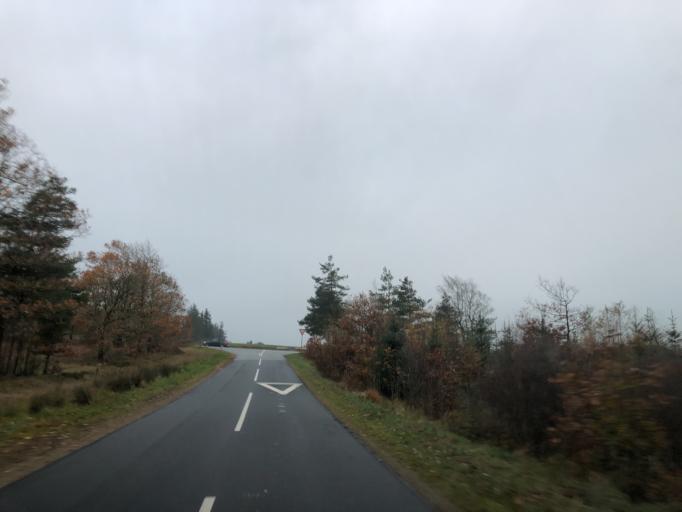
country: DK
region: Central Jutland
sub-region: Ringkobing-Skjern Kommune
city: Videbaek
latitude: 56.1856
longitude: 8.6433
